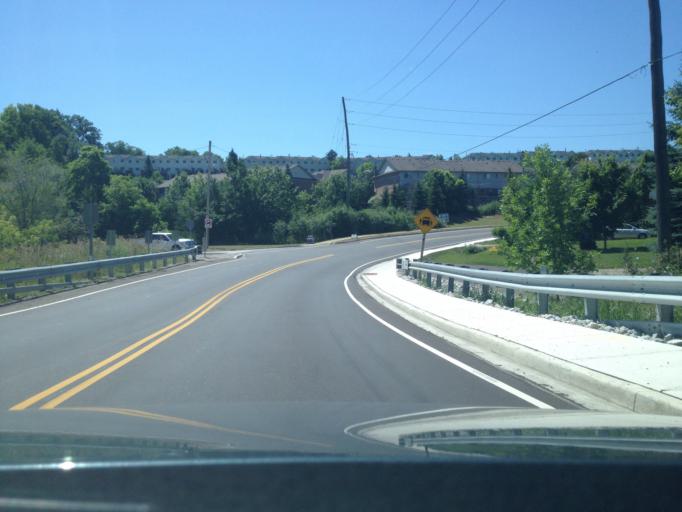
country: CA
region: Ontario
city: Brampton
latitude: 43.6617
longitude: -79.9090
